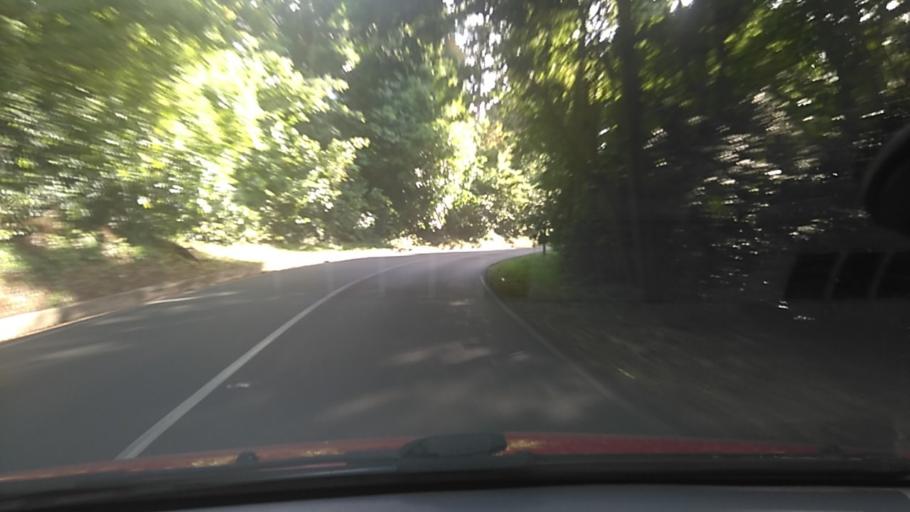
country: MQ
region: Martinique
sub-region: Martinique
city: Ducos
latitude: 14.5733
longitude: -60.9526
